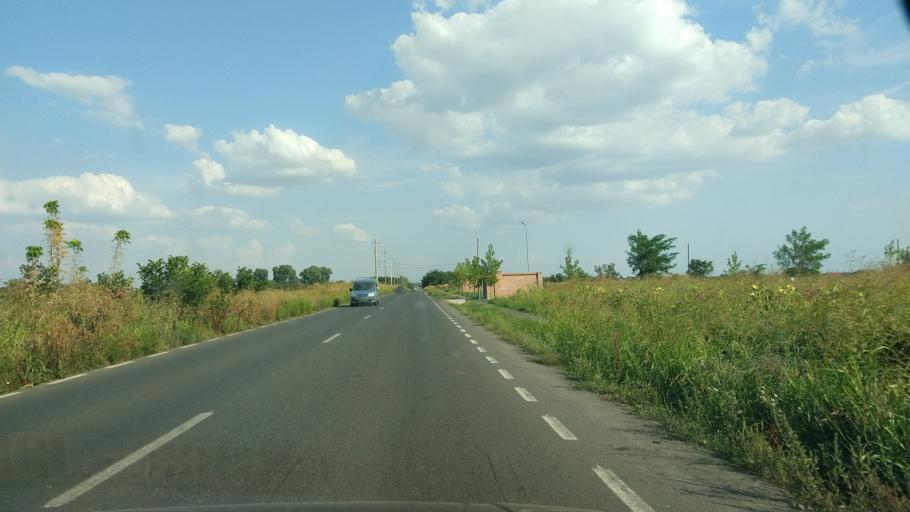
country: RO
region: Ilfov
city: Stefanestii de Jos
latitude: 44.5370
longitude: 26.2224
